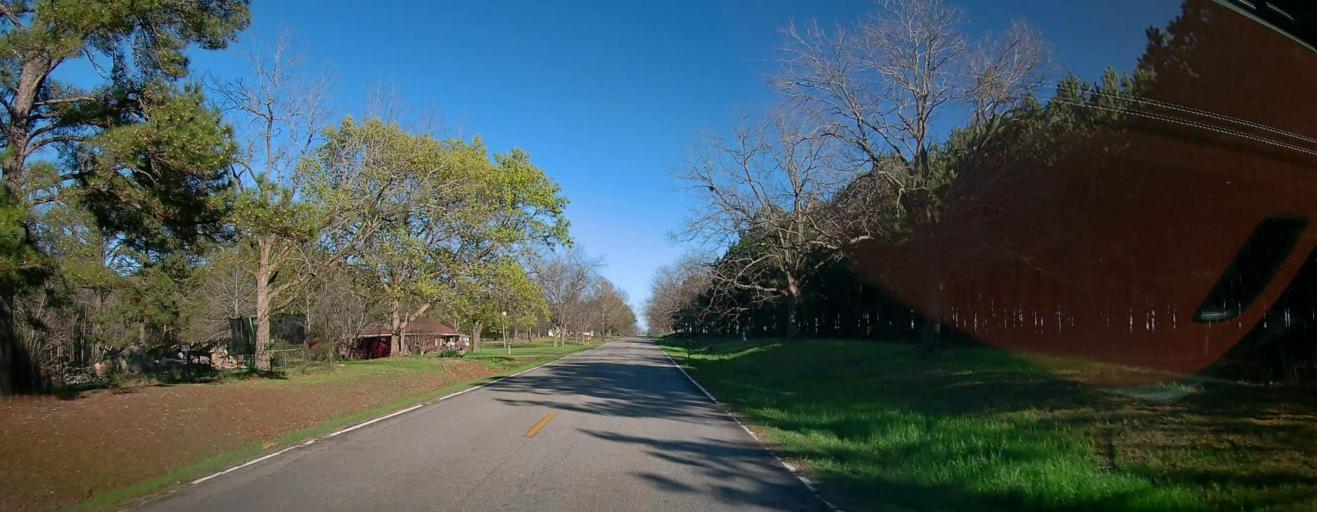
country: US
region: Georgia
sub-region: Houston County
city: Perry
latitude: 32.3743
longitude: -83.7157
